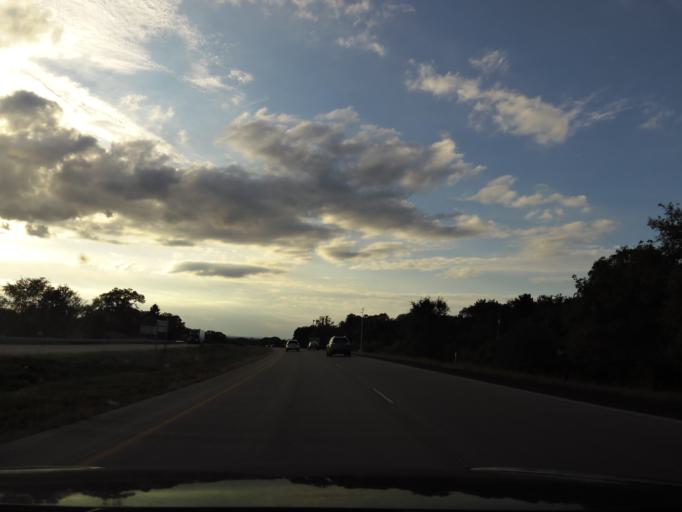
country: US
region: Minnesota
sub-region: Dakota County
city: Hastings
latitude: 44.7940
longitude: -92.8889
